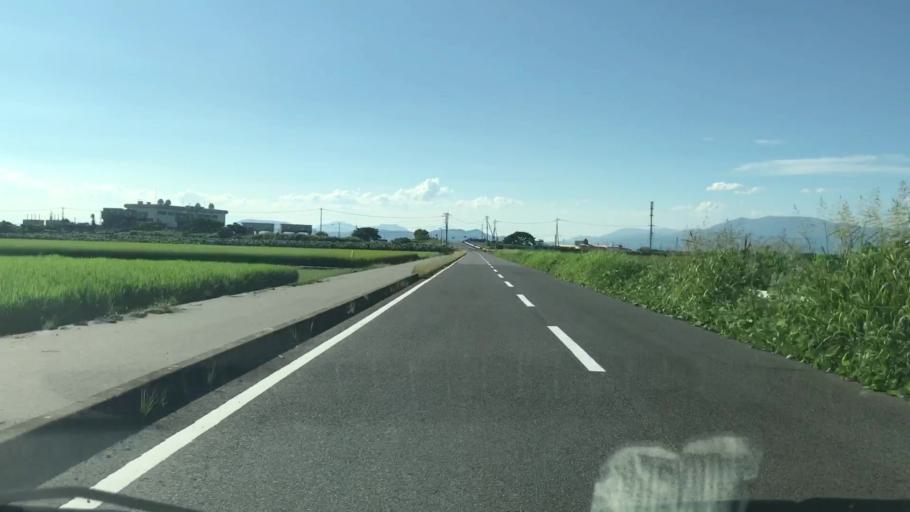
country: JP
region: Saga Prefecture
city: Okawa
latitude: 33.1844
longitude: 130.2949
